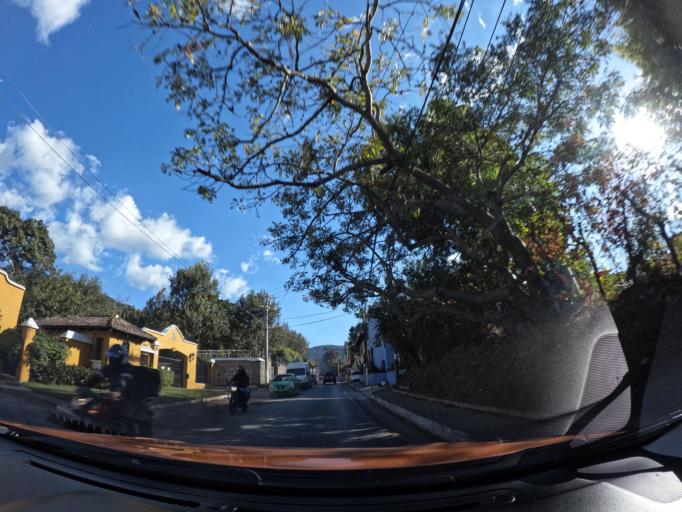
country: GT
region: Sacatepequez
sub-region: Municipio de Santa Maria de Jesus
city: Santa Maria de Jesus
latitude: 14.5320
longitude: -90.7280
